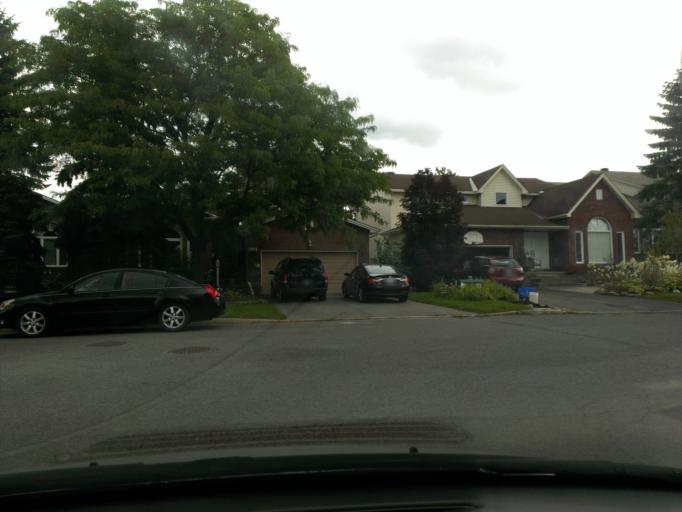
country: CA
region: Quebec
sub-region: Outaouais
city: Gatineau
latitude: 45.4807
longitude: -75.4937
